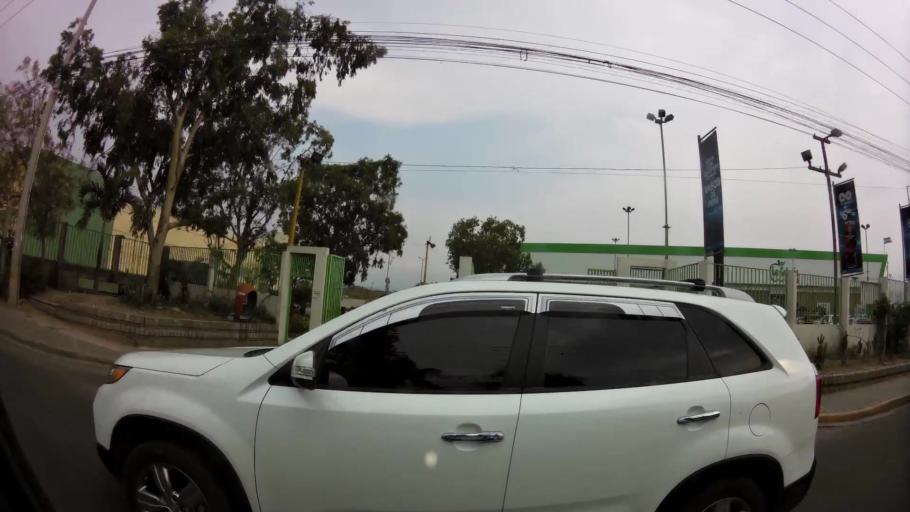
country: HN
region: Francisco Morazan
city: Tegucigalpa
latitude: 14.0635
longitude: -87.2221
